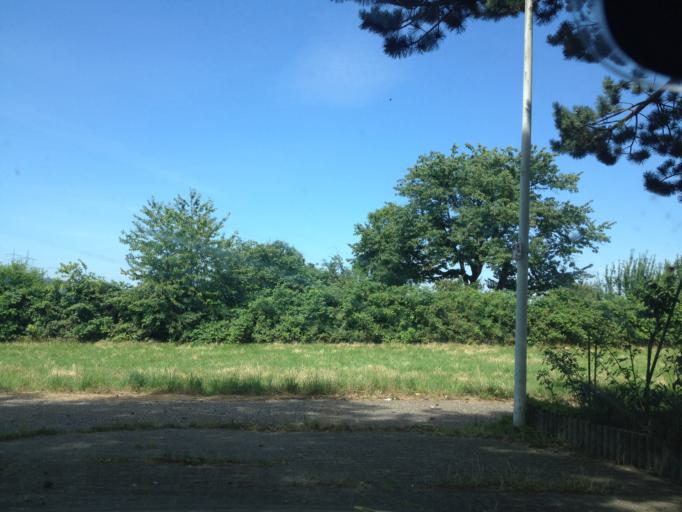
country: DE
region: Baden-Wuerttemberg
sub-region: Regierungsbezirk Stuttgart
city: Leingarten
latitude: 49.1412
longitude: 9.1578
